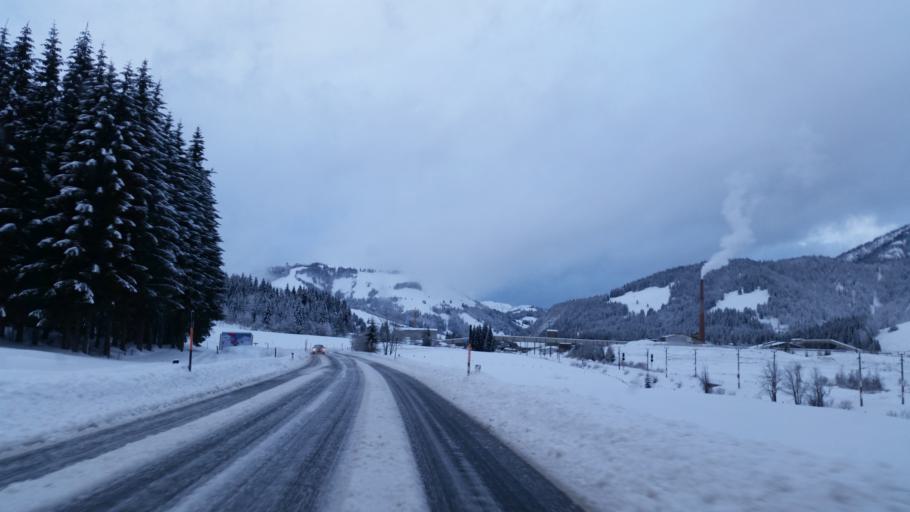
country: AT
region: Tyrol
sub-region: Politischer Bezirk Kitzbuhel
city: Hochfilzen
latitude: 47.4596
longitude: 12.6379
